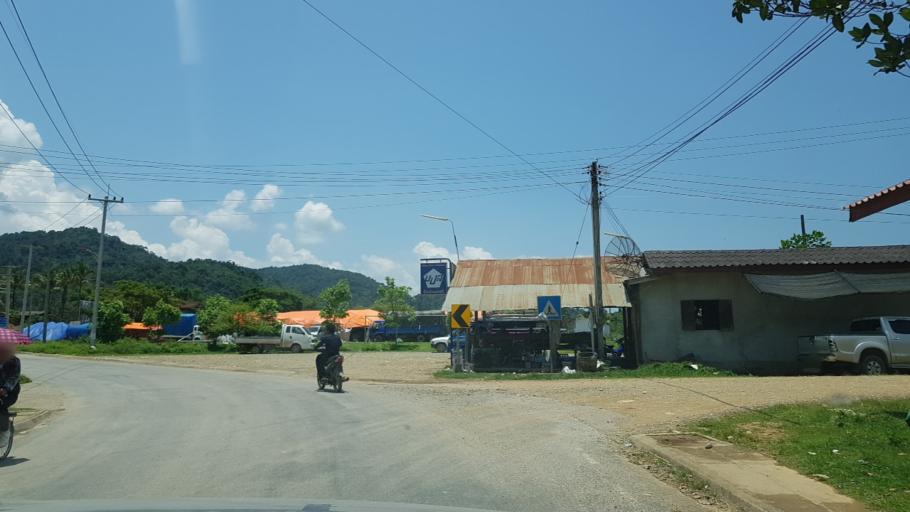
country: LA
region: Vientiane
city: Muang Kasi
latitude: 19.2266
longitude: 102.2520
